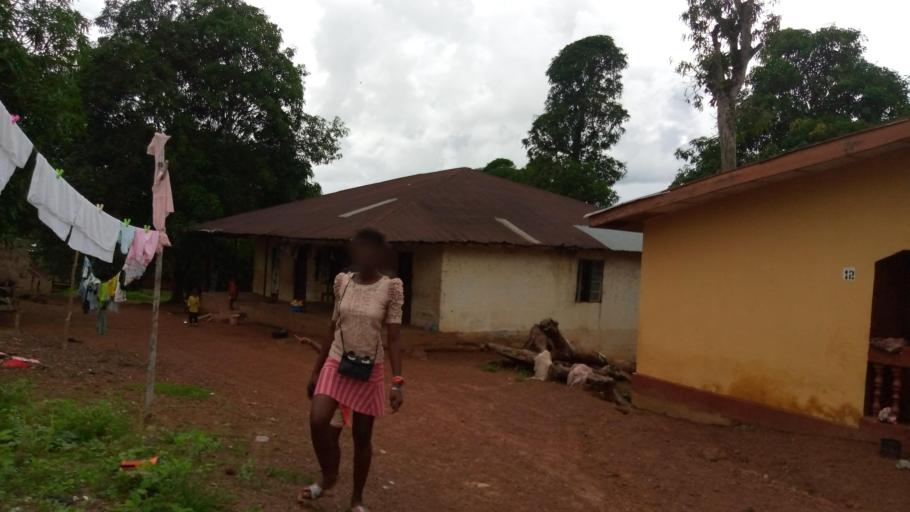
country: SL
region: Southern Province
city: Moyamba
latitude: 8.1643
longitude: -12.4394
